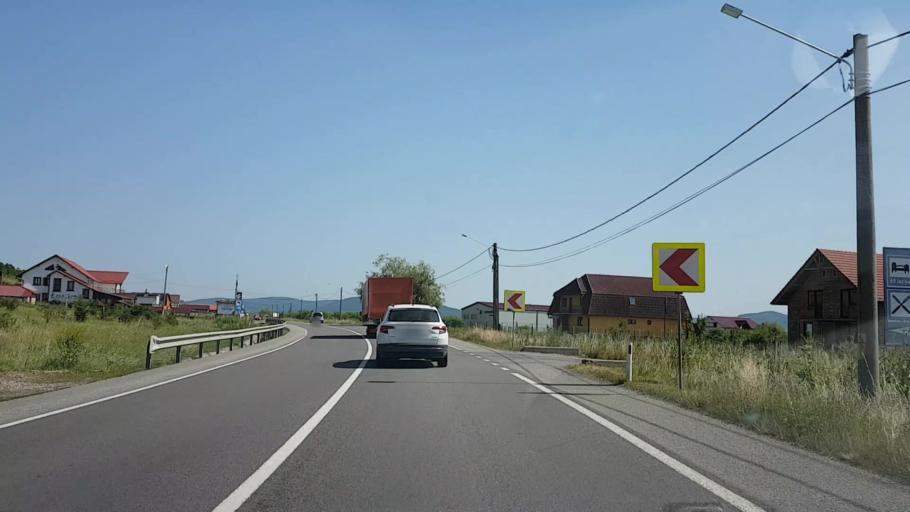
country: RO
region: Bistrita-Nasaud
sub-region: Comuna Sieu-Odorhei
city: Sieu-Odorhei
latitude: 47.1363
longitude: 24.3072
